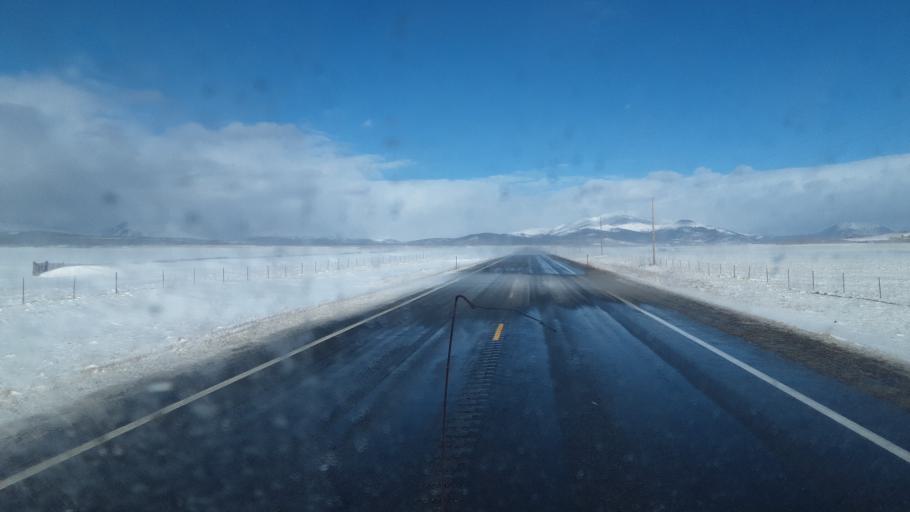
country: US
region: Colorado
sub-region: Park County
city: Fairplay
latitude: 39.1595
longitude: -106.0004
